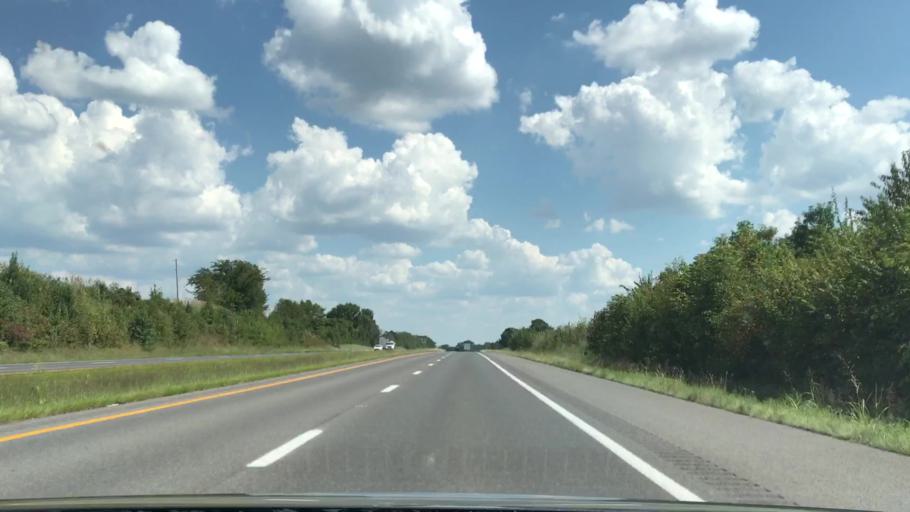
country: US
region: Kentucky
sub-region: Lyon County
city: Eddyville
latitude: 37.1082
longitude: -87.9998
